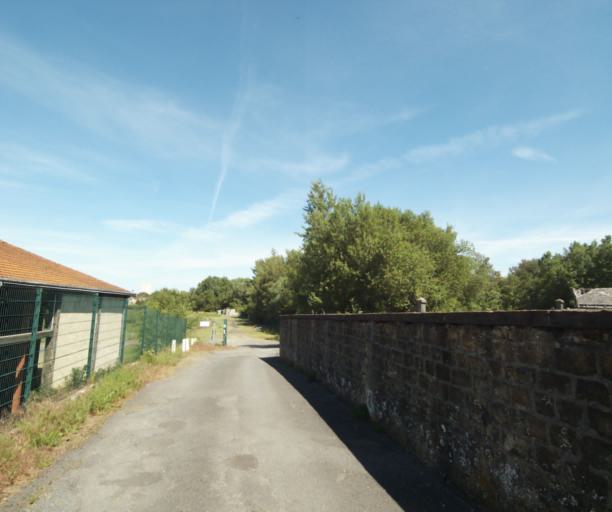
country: FR
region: Champagne-Ardenne
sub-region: Departement des Ardennes
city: Charleville-Mezieres
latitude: 49.7547
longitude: 4.7314
